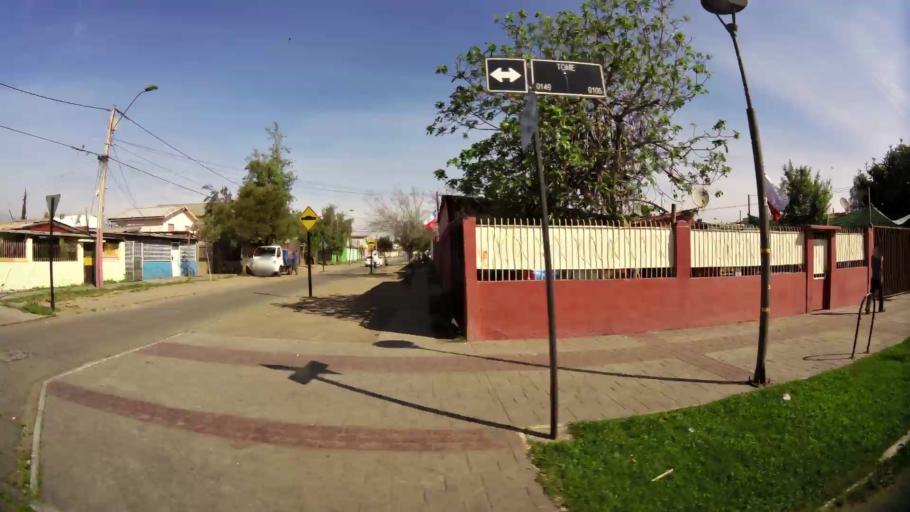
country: CL
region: Santiago Metropolitan
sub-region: Provincia de Santiago
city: La Pintana
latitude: -33.5328
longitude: -70.6313
